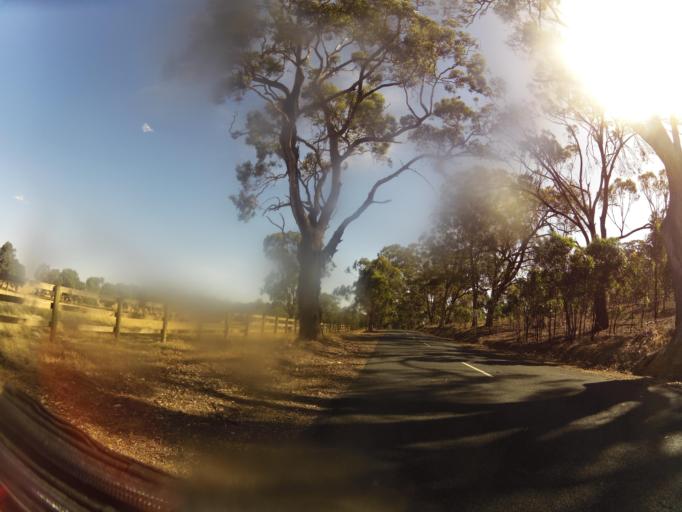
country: AU
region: Victoria
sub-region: Murrindindi
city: Kinglake West
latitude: -36.8966
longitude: 145.1076
